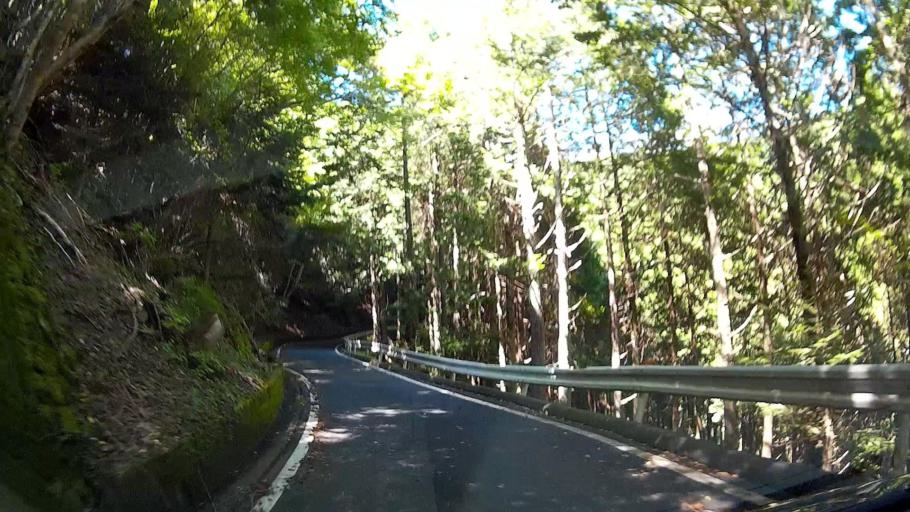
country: JP
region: Shizuoka
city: Shizuoka-shi
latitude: 35.1959
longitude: 138.2649
